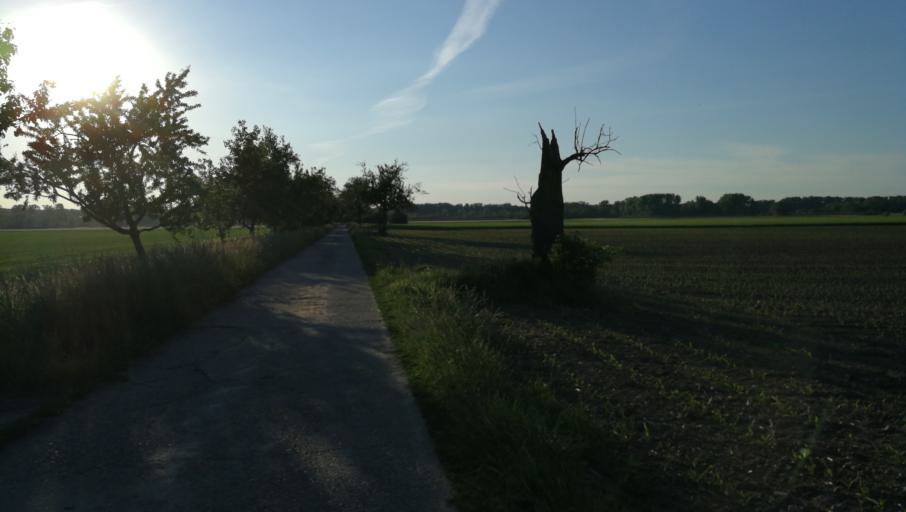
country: DE
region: Baden-Wuerttemberg
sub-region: Karlsruhe Region
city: Ketsch
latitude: 49.3440
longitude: 8.5015
